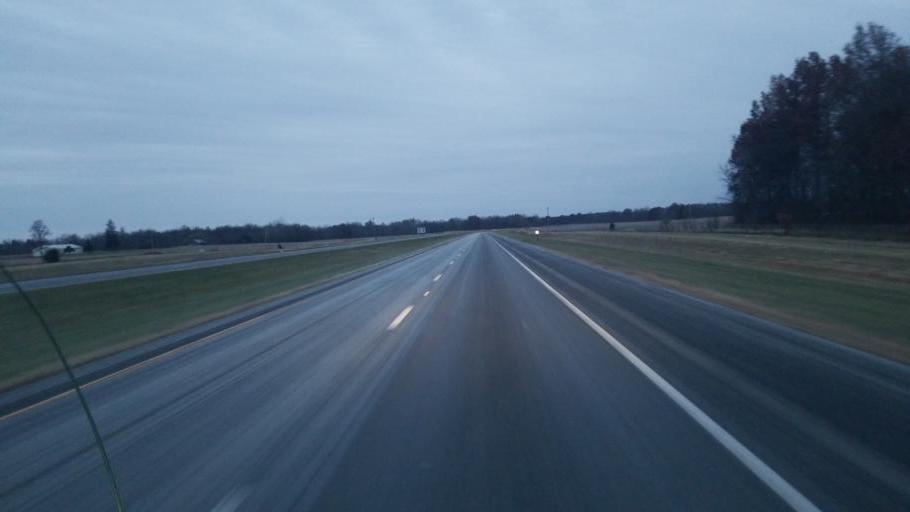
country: US
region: Ohio
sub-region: Hardin County
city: Forest
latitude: 40.8242
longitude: -83.5386
